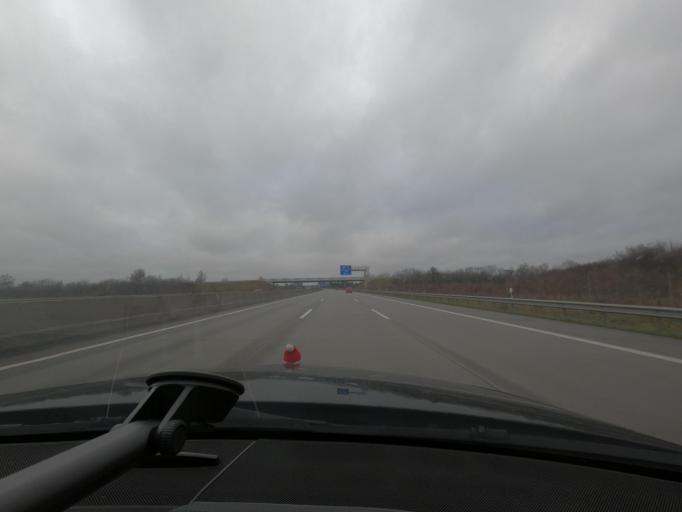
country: DE
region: Schleswig-Holstein
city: Padenstedt
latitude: 54.0306
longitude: 9.9326
